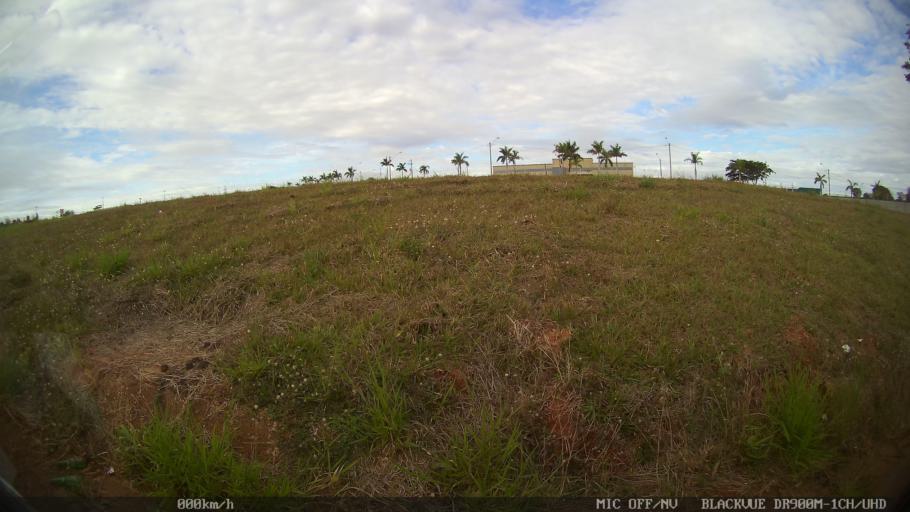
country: BR
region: Sao Paulo
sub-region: Sao Jose Do Rio Preto
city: Sao Jose do Rio Preto
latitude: -20.8238
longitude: -49.4174
